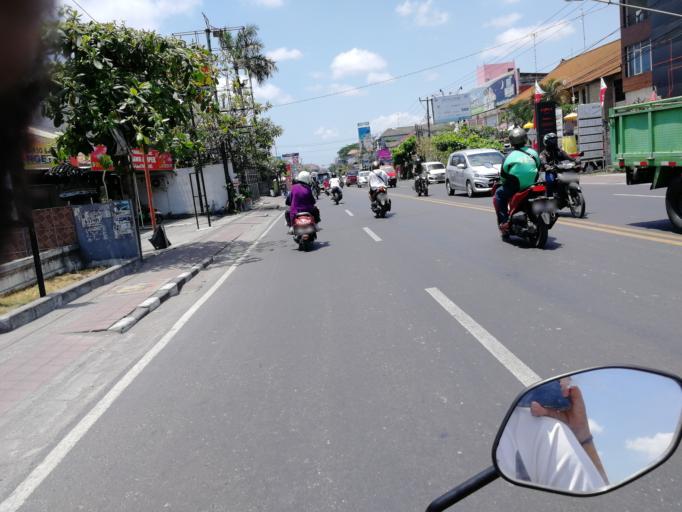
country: ID
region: Bali
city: Banjar Kertasari
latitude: -8.6390
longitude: 115.1965
